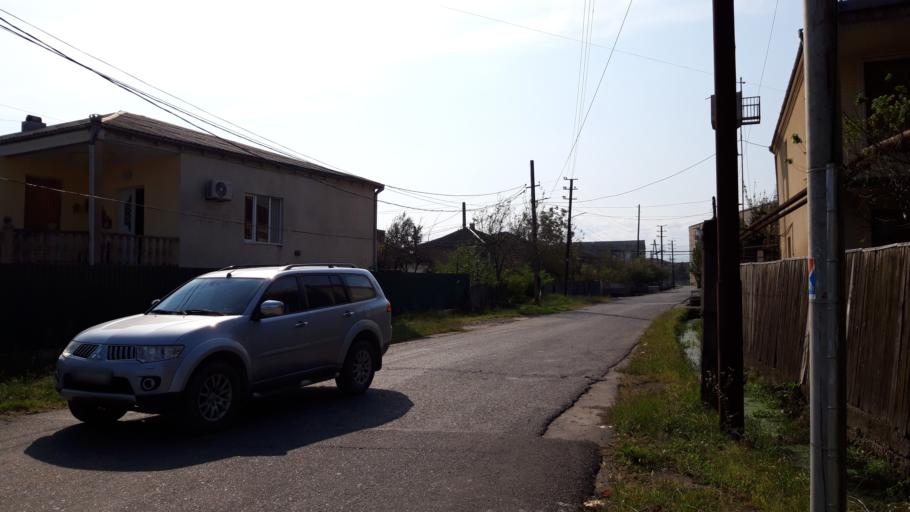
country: GE
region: Imereti
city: Samtredia
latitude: 42.1622
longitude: 42.3342
